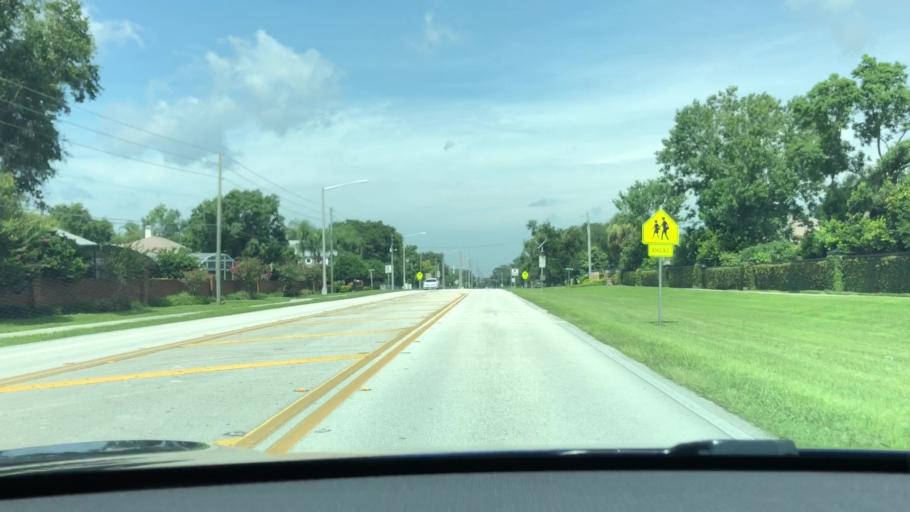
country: US
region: Florida
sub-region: Orange County
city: Conway
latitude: 28.4951
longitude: -81.3251
